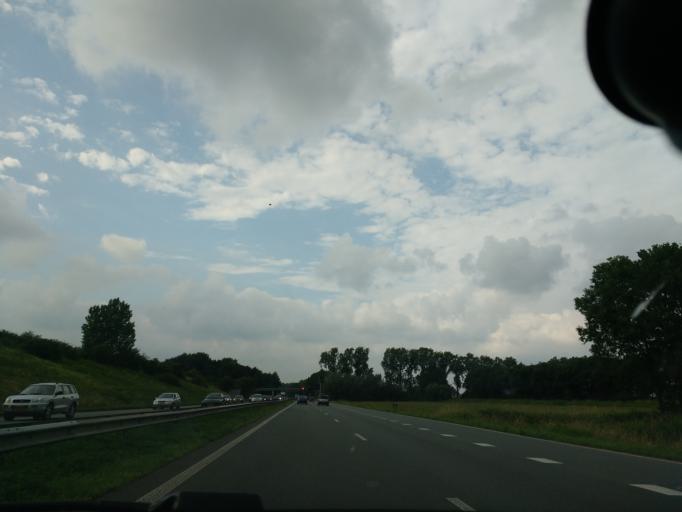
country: NL
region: Gelderland
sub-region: Gemeente Overbetuwe
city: Elst
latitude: 51.9362
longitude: 5.8780
